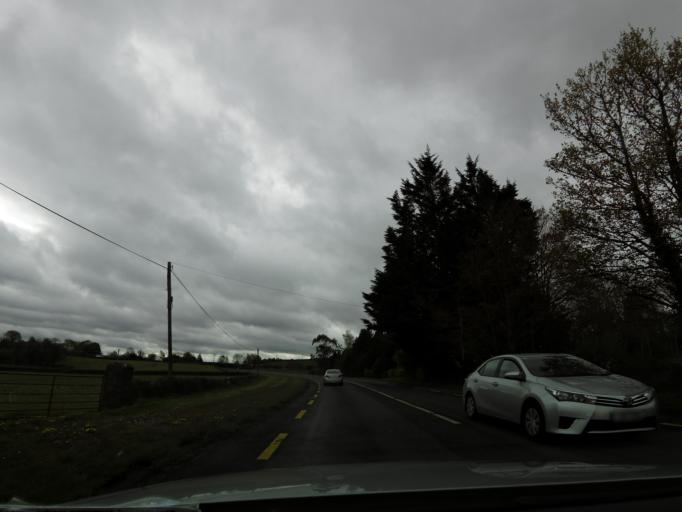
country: IE
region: Leinster
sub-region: Kilkenny
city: Kilkenny
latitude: 52.6795
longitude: -7.2751
